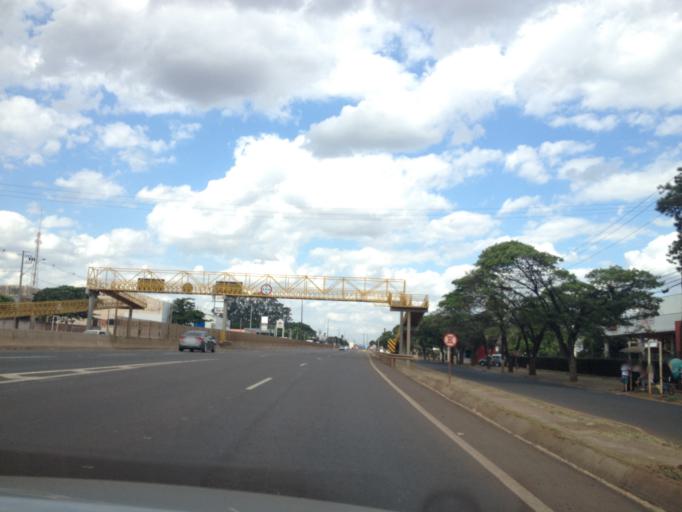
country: BR
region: Parana
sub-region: Sarandi
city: Sarandi
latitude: -23.4338
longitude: -51.8847
